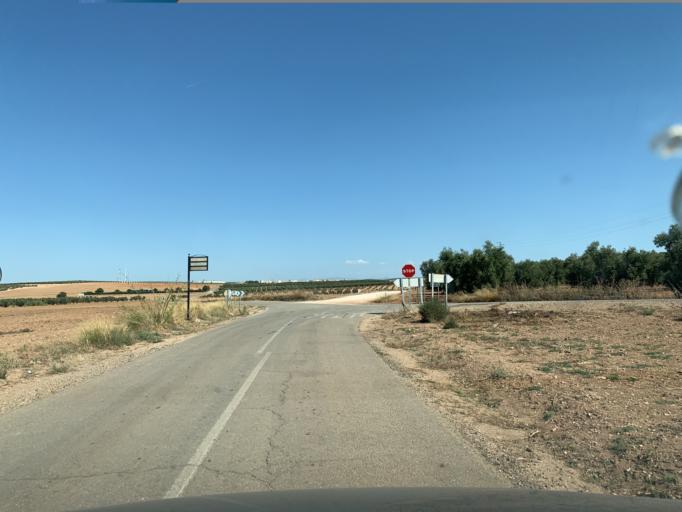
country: ES
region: Andalusia
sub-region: Provincia de Sevilla
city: El Rubio
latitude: 37.3472
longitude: -5.0121
